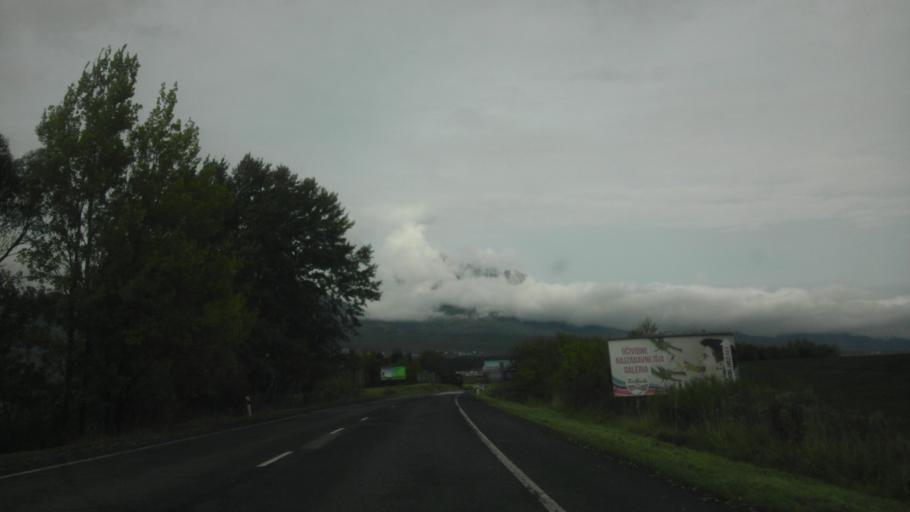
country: SK
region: Presovsky
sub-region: Okres Poprad
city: Nova Lesna
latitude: 49.0900
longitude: 20.2618
